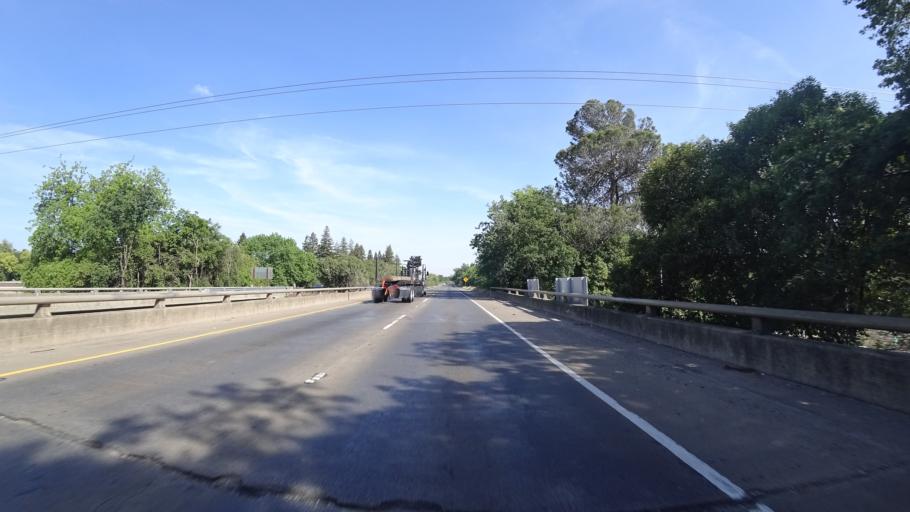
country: US
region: California
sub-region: Butte County
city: Chico
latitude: 39.7363
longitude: -121.8195
